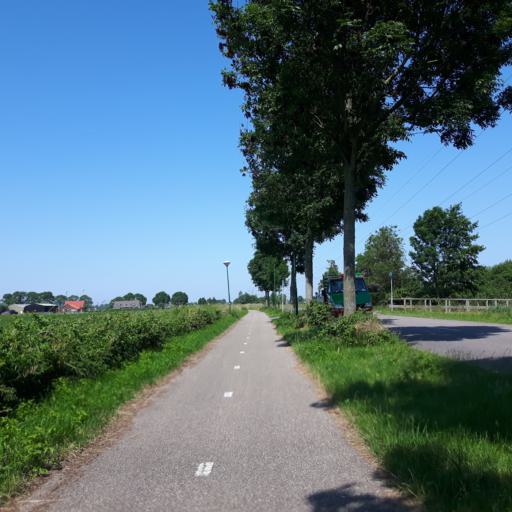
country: NL
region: Utrecht
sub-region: Gemeente Utrecht
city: Utrecht
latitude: 52.1350
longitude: 5.1089
